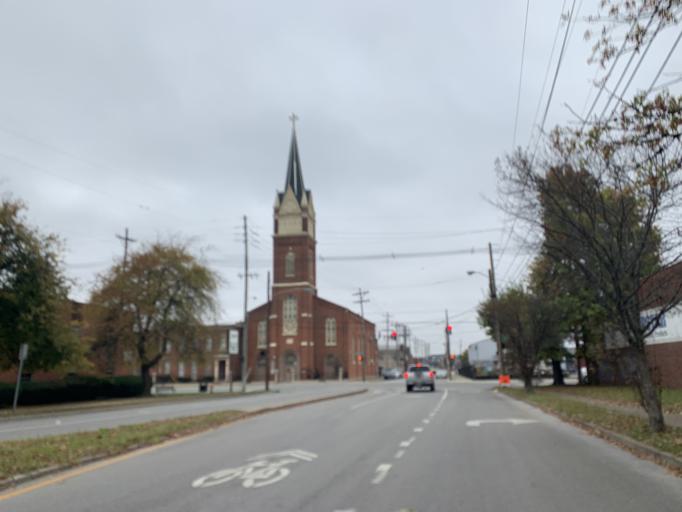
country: US
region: Kentucky
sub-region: Jefferson County
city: Louisville
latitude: 38.2563
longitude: -85.7717
